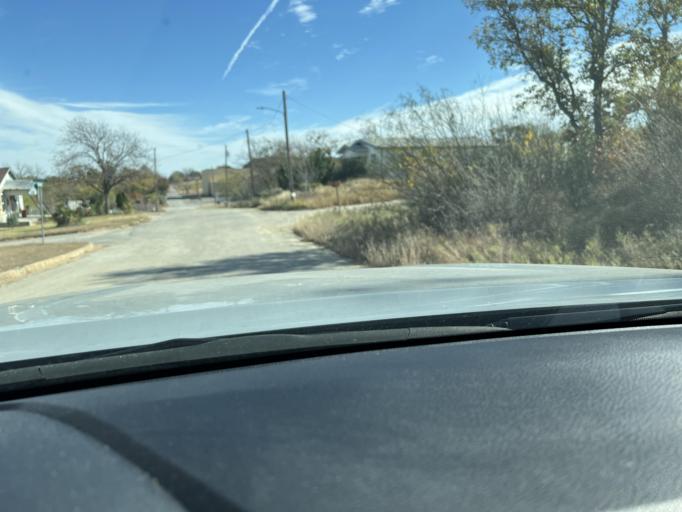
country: US
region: Texas
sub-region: Eastland County
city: Eastland
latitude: 32.3996
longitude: -98.8324
